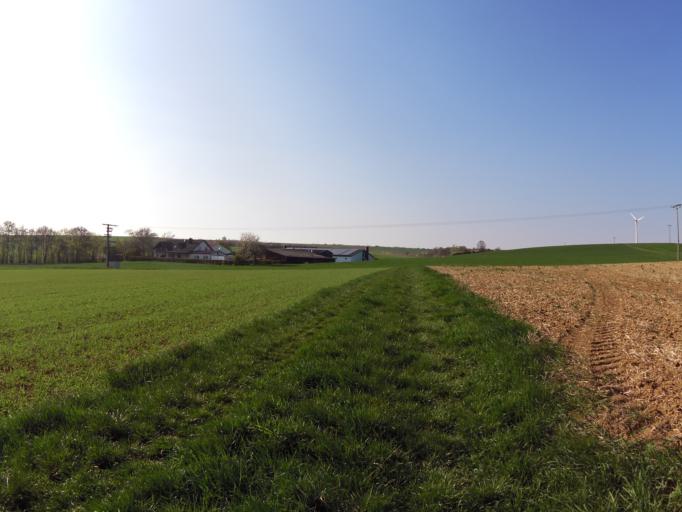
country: DE
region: Bavaria
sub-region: Regierungsbezirk Unterfranken
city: Theilheim
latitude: 49.7638
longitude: 10.0383
